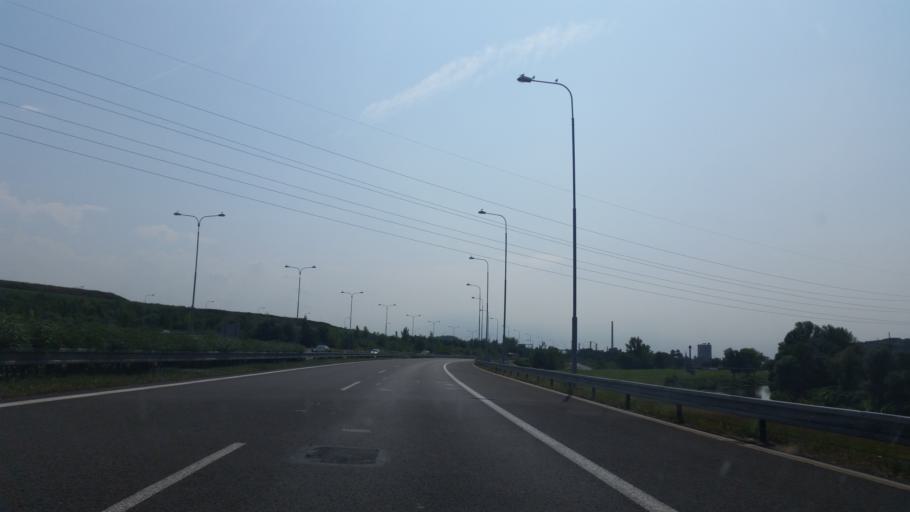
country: CZ
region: Moravskoslezsky
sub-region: Okres Ostrava-Mesto
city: Ostrava
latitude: 49.8782
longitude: 18.3037
